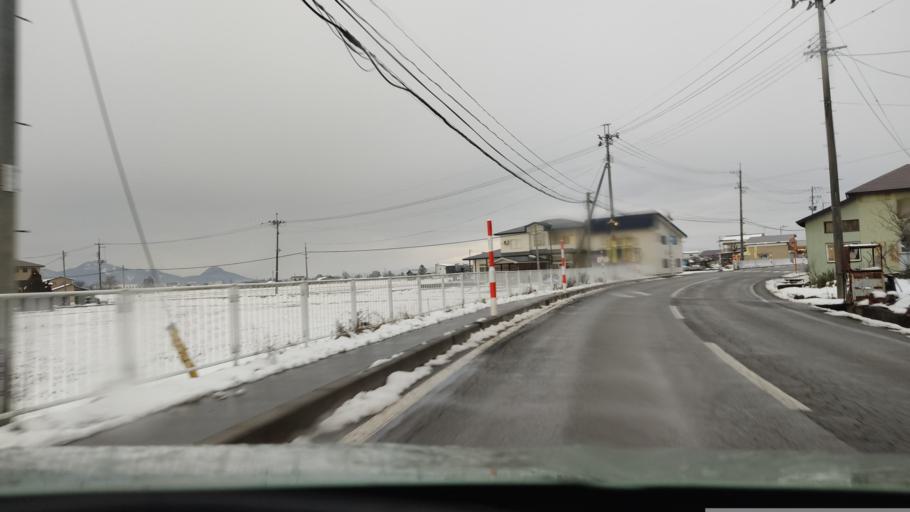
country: JP
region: Akita
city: Omagari
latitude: 39.4301
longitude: 140.5245
